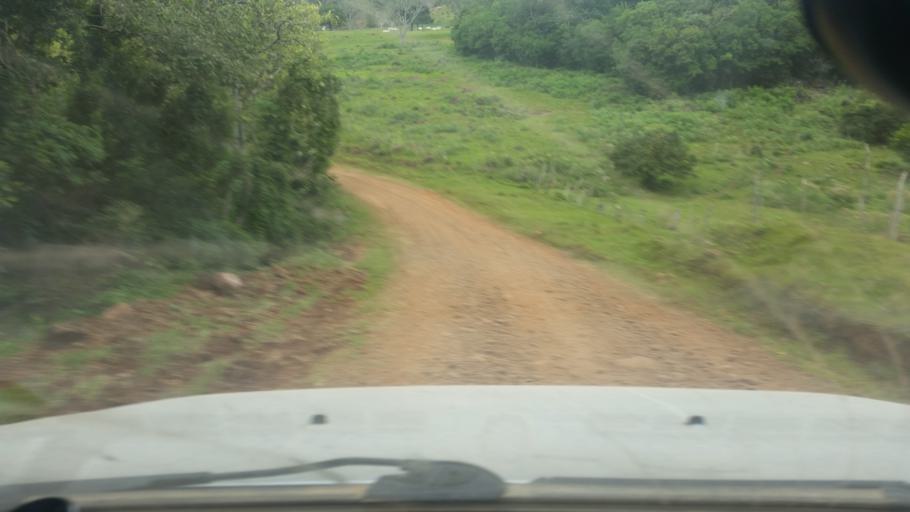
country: PY
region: Guaira
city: Independencia
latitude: -25.8096
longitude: -56.2767
